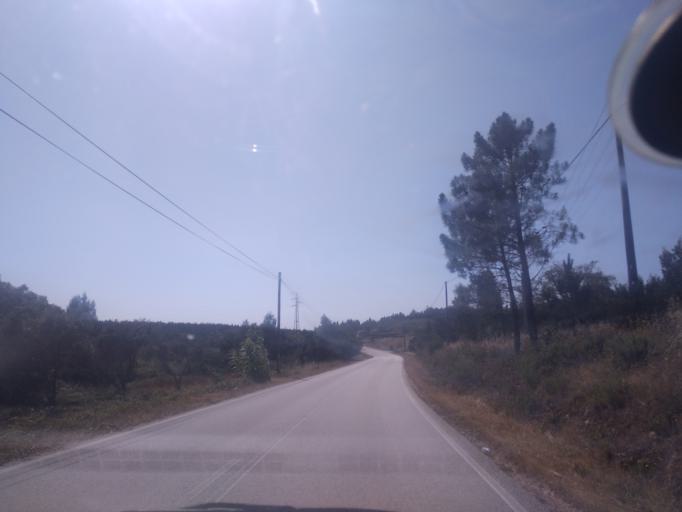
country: PT
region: Faro
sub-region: Aljezur
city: Aljezur
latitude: 37.2193
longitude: -8.7940
